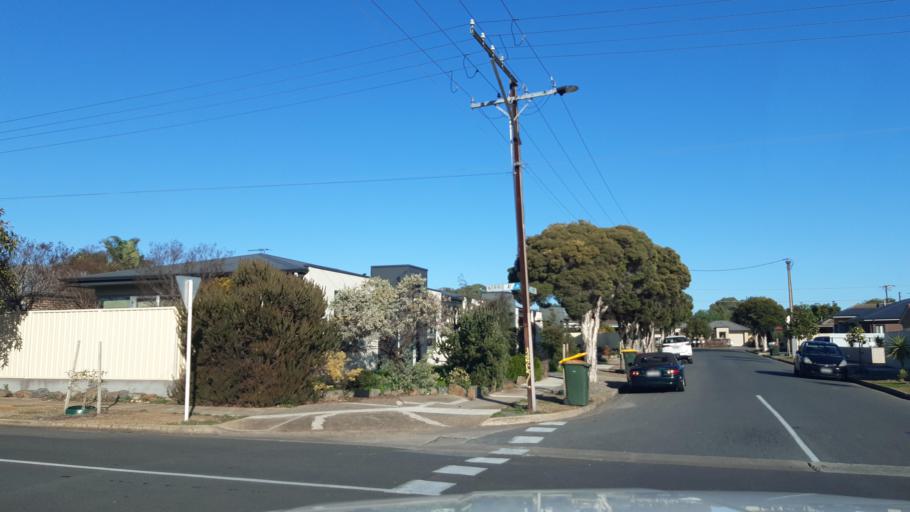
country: AU
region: South Australia
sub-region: Marion
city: Clovelly Park
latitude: -34.9963
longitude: 138.5674
